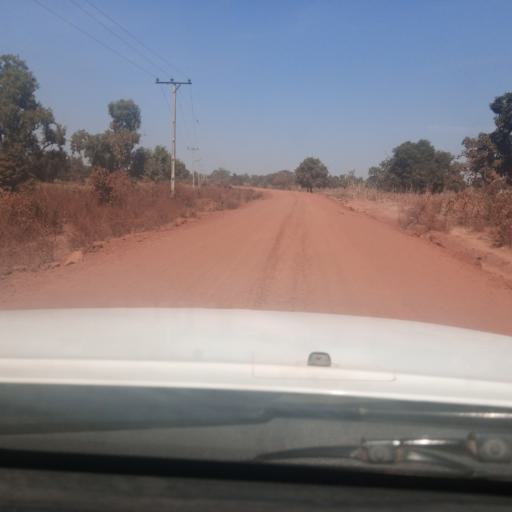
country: NG
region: Adamawa
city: Yola
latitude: 9.2052
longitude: 12.8779
